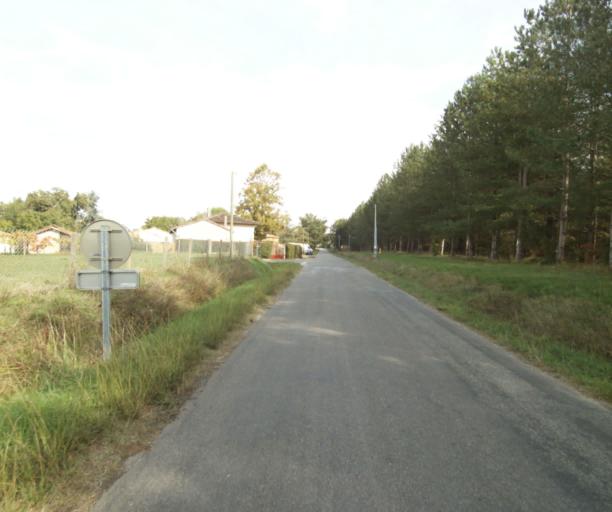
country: FR
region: Midi-Pyrenees
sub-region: Departement du Tarn-et-Garonne
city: Orgueil
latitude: 43.9012
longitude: 1.4022
